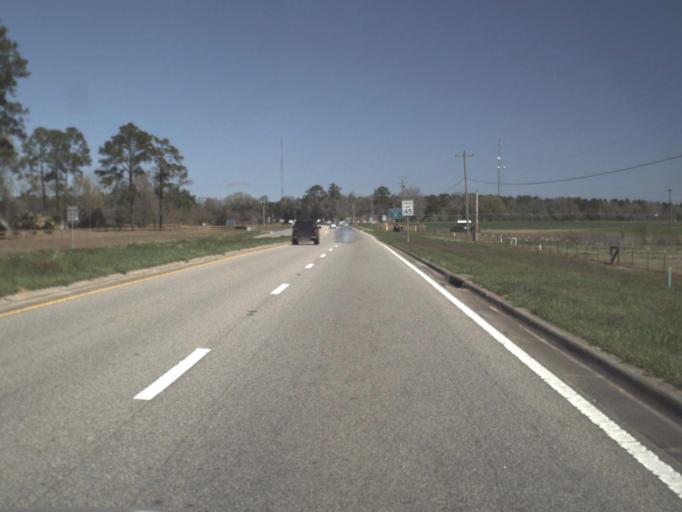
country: US
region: Florida
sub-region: Gadsden County
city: Quincy
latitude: 30.5431
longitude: -84.5935
